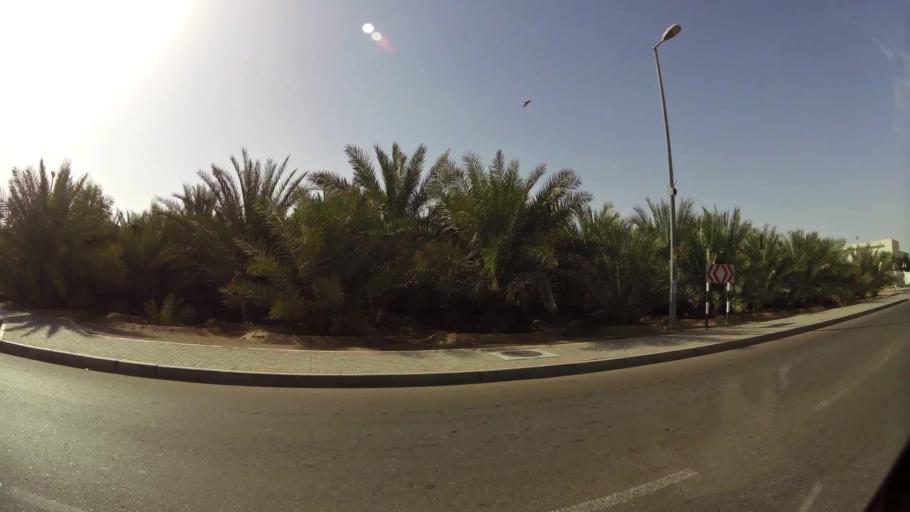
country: OM
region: Al Buraimi
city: Al Buraymi
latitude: 24.3477
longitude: 55.7917
